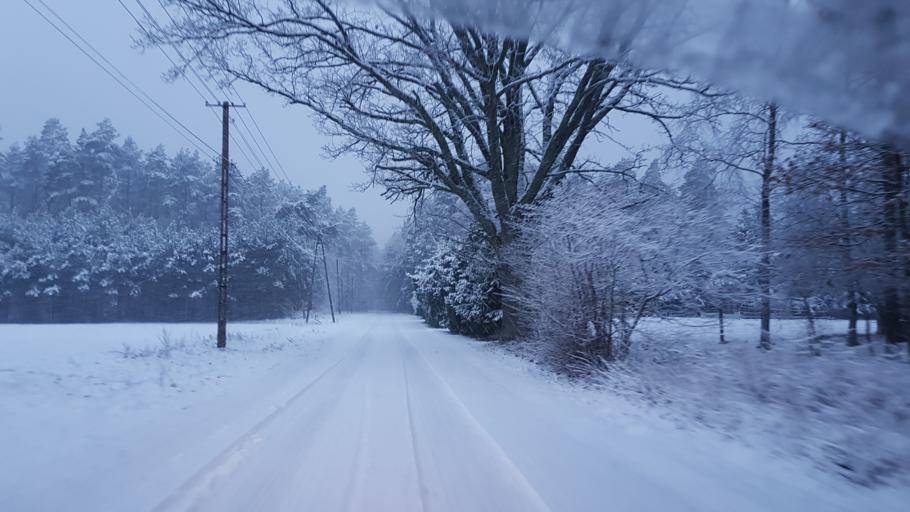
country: PL
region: West Pomeranian Voivodeship
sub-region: Powiat koszalinski
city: Polanow
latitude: 54.1692
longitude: 16.4928
